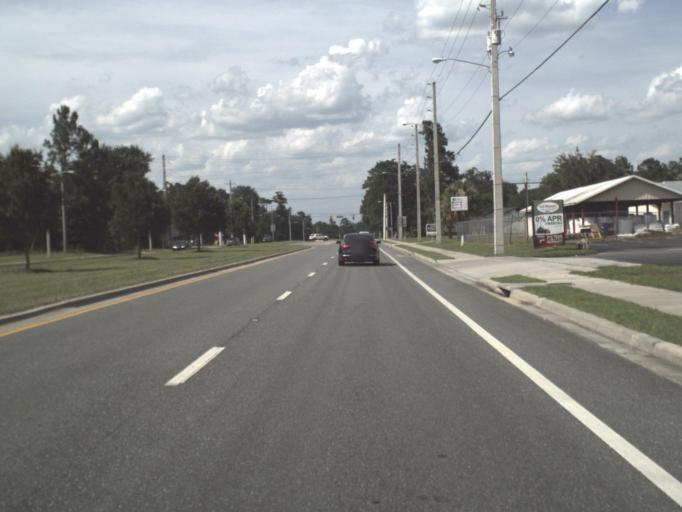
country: US
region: Florida
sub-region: Columbia County
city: Lake City
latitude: 30.1617
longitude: -82.6446
